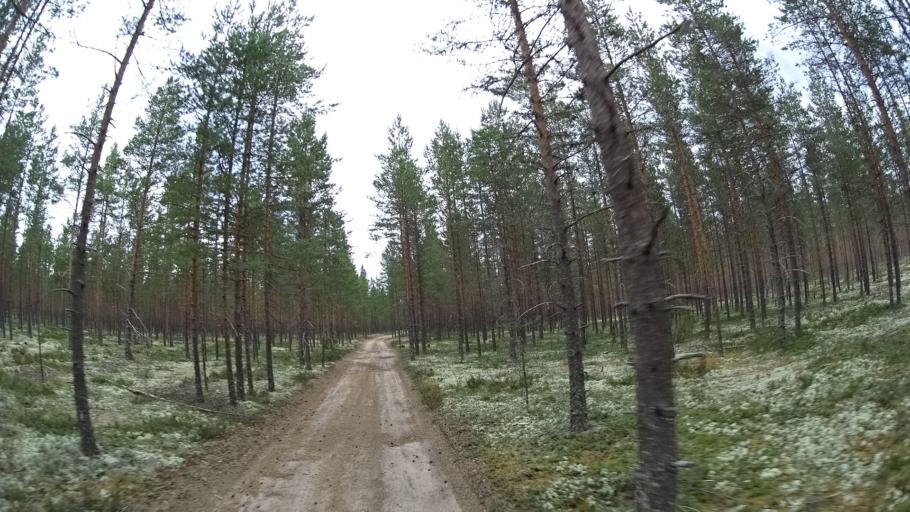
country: FI
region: Satakunta
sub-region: Pohjois-Satakunta
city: Jaemijaervi
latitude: 61.7651
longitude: 22.7869
